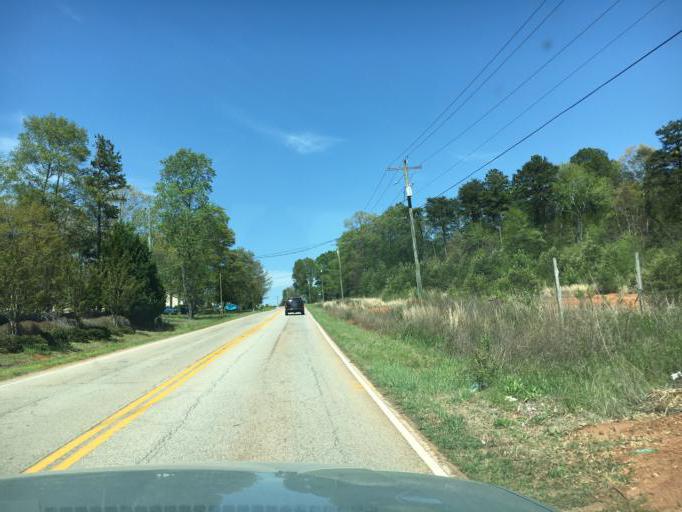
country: US
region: South Carolina
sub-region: Greenville County
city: Greer
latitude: 34.9765
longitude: -82.2277
